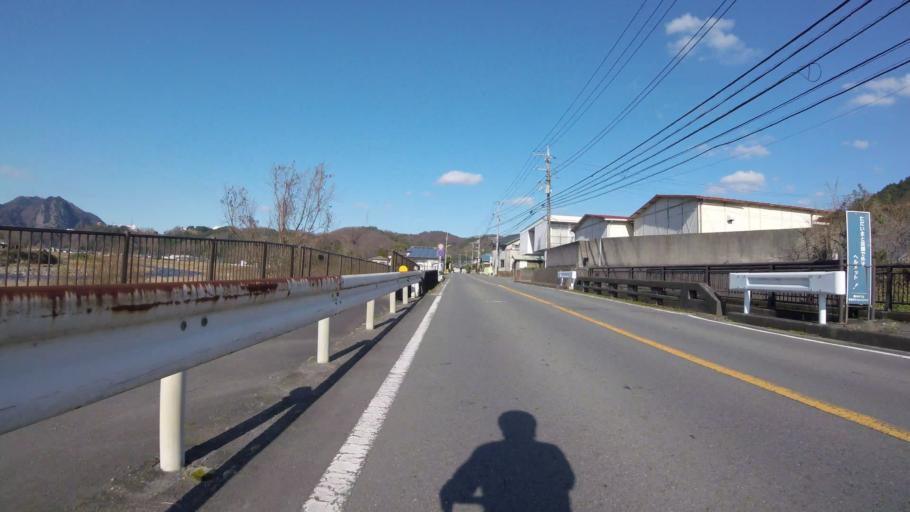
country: JP
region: Shizuoka
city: Ito
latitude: 34.9864
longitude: 138.9534
